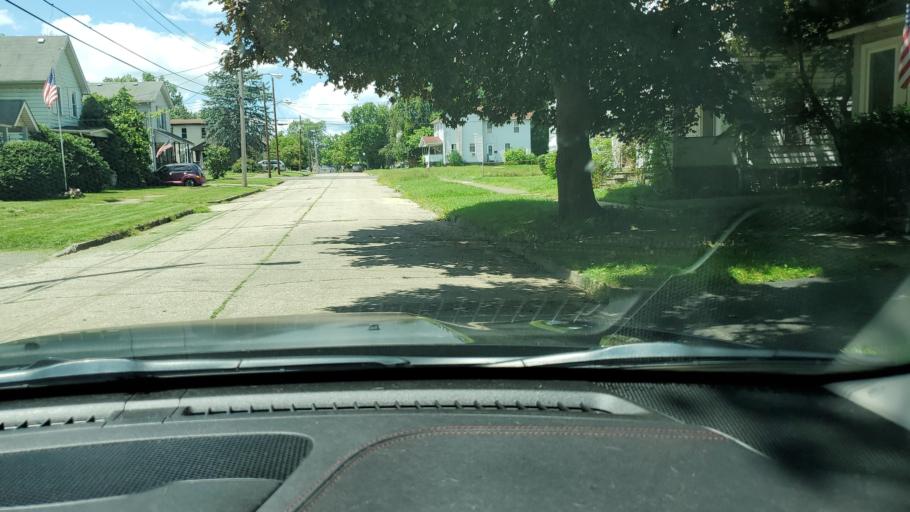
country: US
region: Ohio
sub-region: Trumbull County
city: Niles
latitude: 41.1852
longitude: -80.7671
